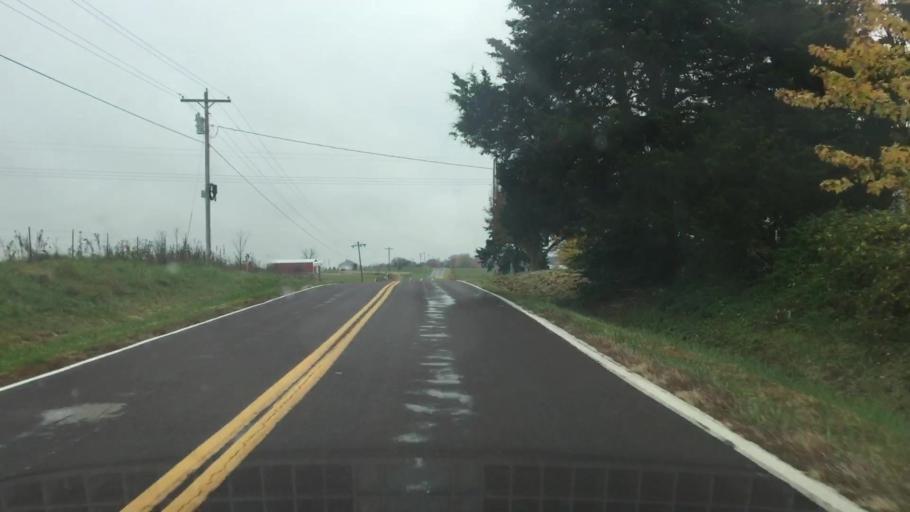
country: US
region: Missouri
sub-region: Callaway County
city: Fulton
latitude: 38.8330
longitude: -91.9191
